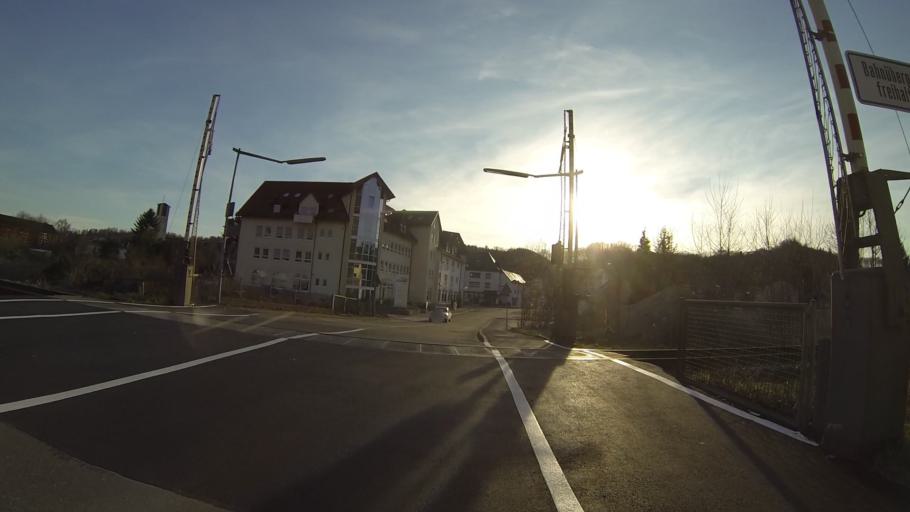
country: DE
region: Baden-Wuerttemberg
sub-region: Regierungsbezirk Stuttgart
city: Heidenheim an der Brenz
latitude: 48.6586
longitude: 10.1592
